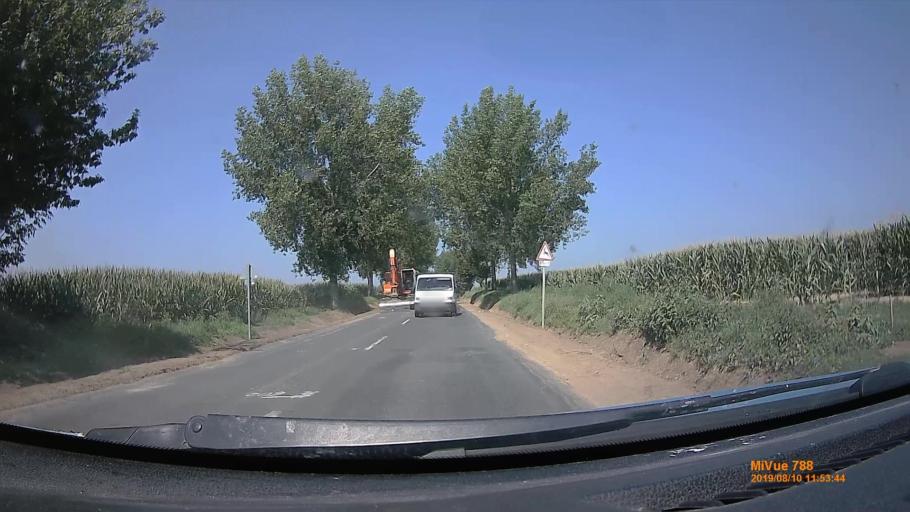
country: HU
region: Somogy
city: Somogyvar
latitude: 46.5158
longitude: 17.6931
